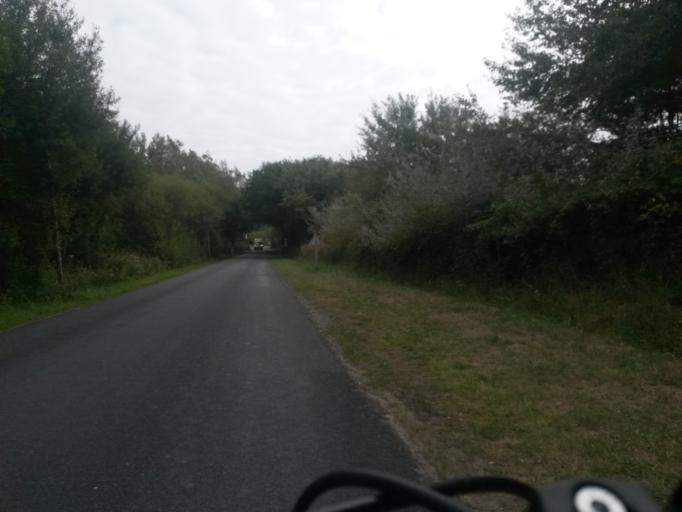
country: FR
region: Poitou-Charentes
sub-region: Departement de la Charente-Maritime
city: Saint-Denis-d'Oleron
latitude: 46.0076
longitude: -1.3861
